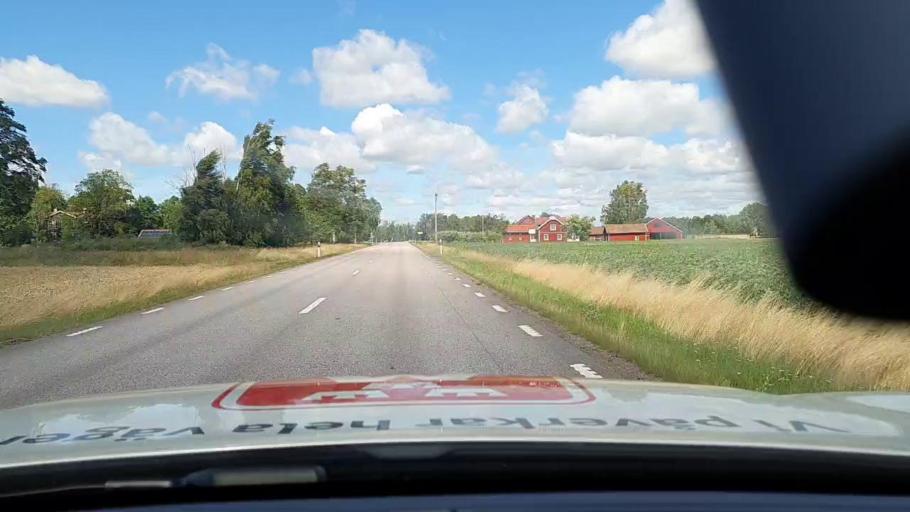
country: SE
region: Vaestra Goetaland
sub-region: Skovde Kommun
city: Stopen
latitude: 58.5484
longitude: 14.0025
